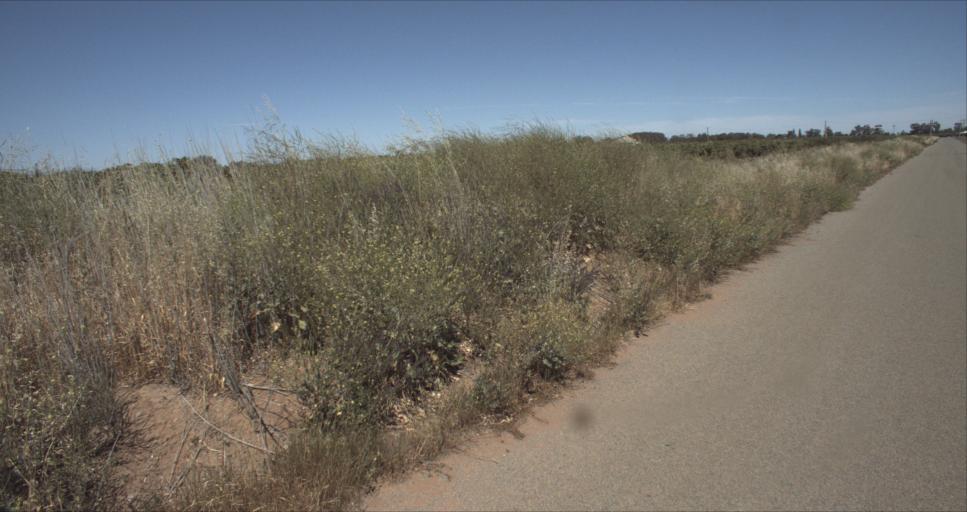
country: AU
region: New South Wales
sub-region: Leeton
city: Leeton
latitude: -34.5342
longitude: 146.3527
